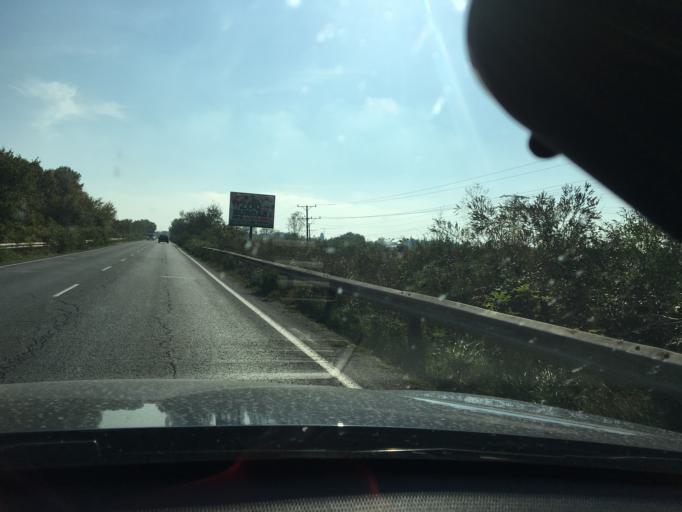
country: BG
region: Burgas
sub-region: Obshtina Nesebur
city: Ravda
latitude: 42.6691
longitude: 27.6951
